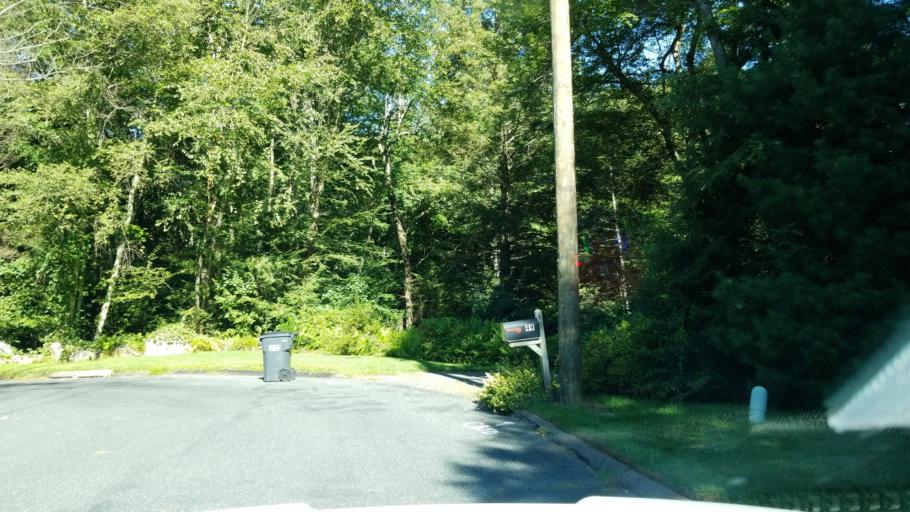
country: US
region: Connecticut
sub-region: Tolland County
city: Somers
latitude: 41.9792
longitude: -72.4162
